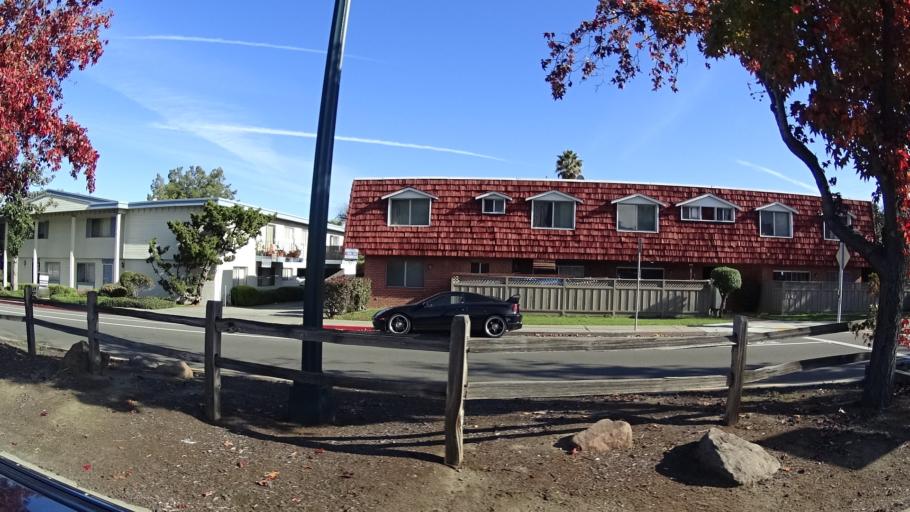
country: US
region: California
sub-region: Santa Clara County
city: Cupertino
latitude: 37.3397
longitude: -122.0415
